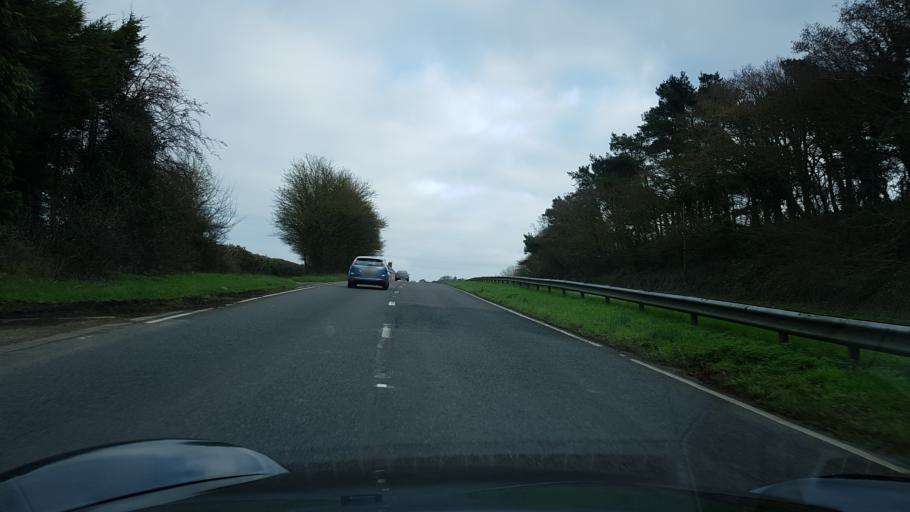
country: GB
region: England
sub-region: Dorset
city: Bridport
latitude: 50.7309
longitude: -2.6857
